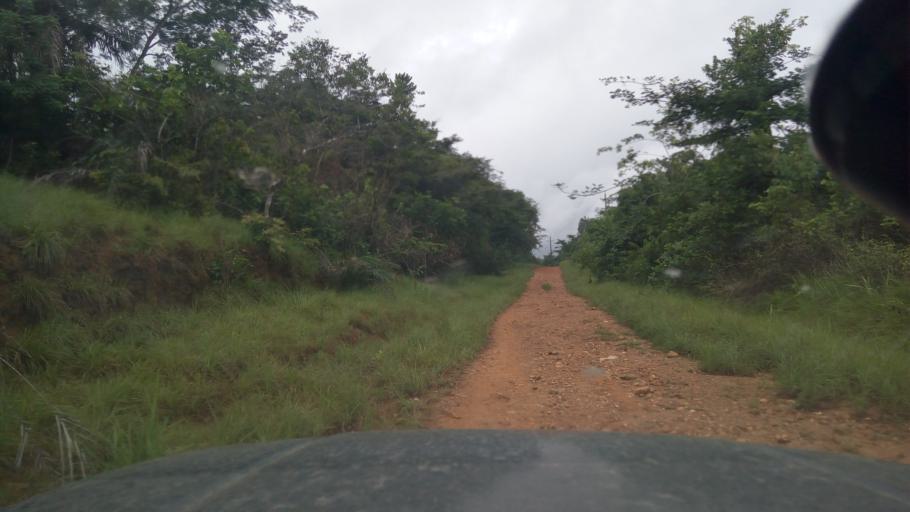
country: SL
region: Eastern Province
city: Boajibu
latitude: 8.1428
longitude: -11.2521
